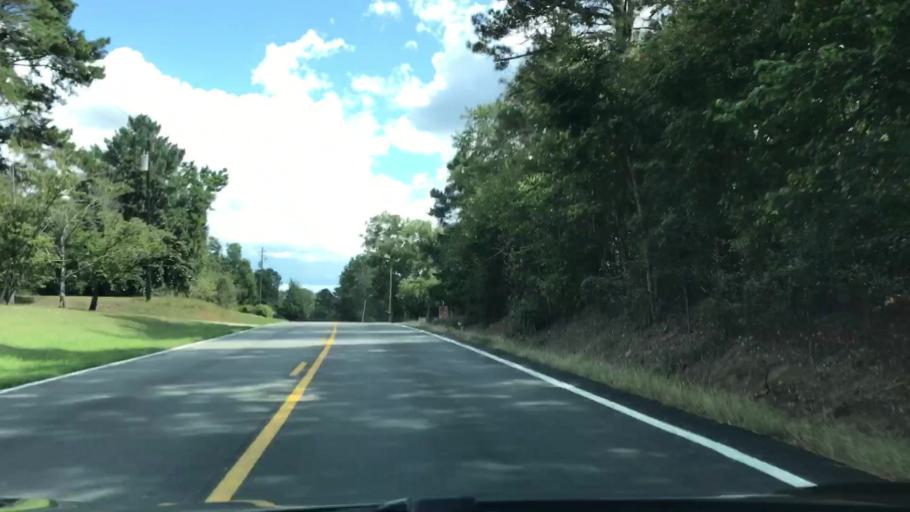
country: US
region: Georgia
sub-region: Greene County
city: Greensboro
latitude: 33.5682
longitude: -83.1616
